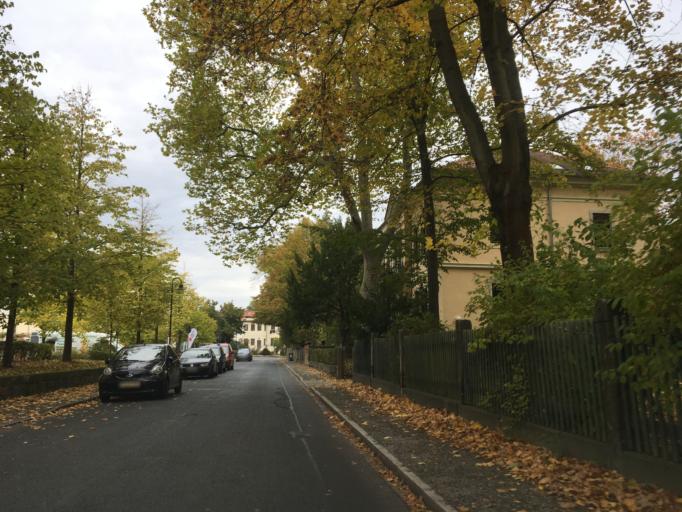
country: DE
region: Saxony
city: Ottendorf-Okrilla
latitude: 51.1237
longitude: 13.8463
